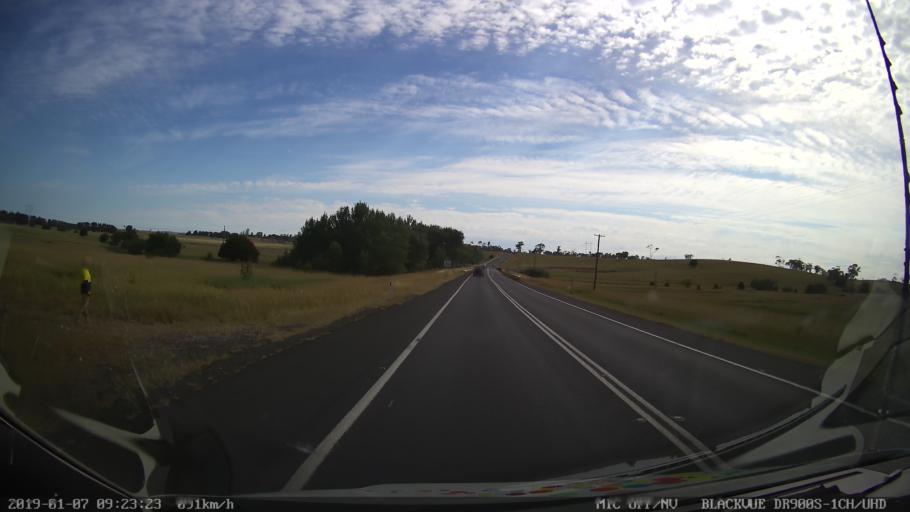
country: AU
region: New South Wales
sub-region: Armidale Dumaresq
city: Armidale
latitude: -30.5570
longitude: 151.5845
